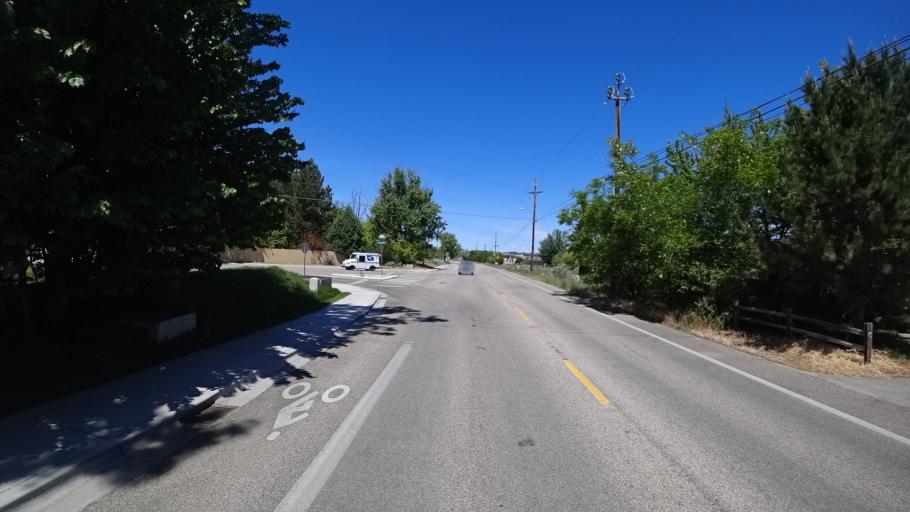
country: US
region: Idaho
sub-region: Ada County
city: Boise
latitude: 43.5711
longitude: -116.1528
